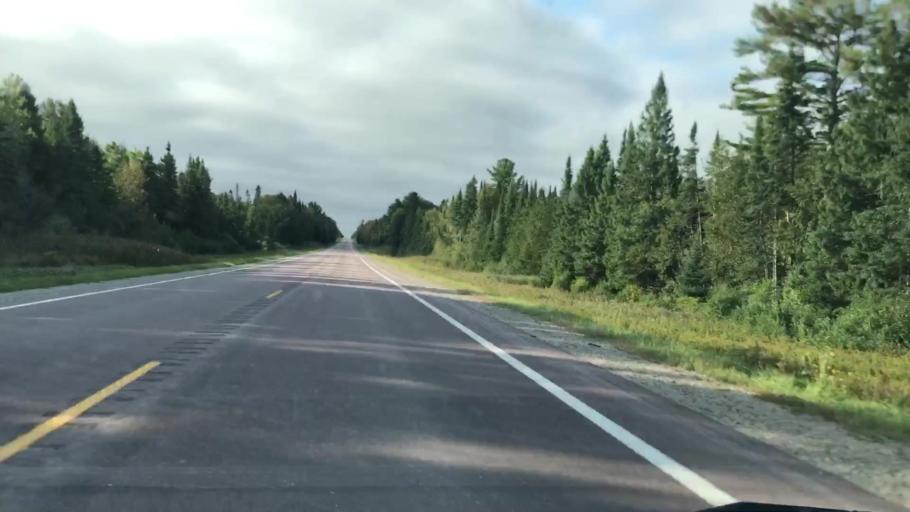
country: US
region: Michigan
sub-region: Luce County
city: Newberry
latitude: 46.2974
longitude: -85.5689
